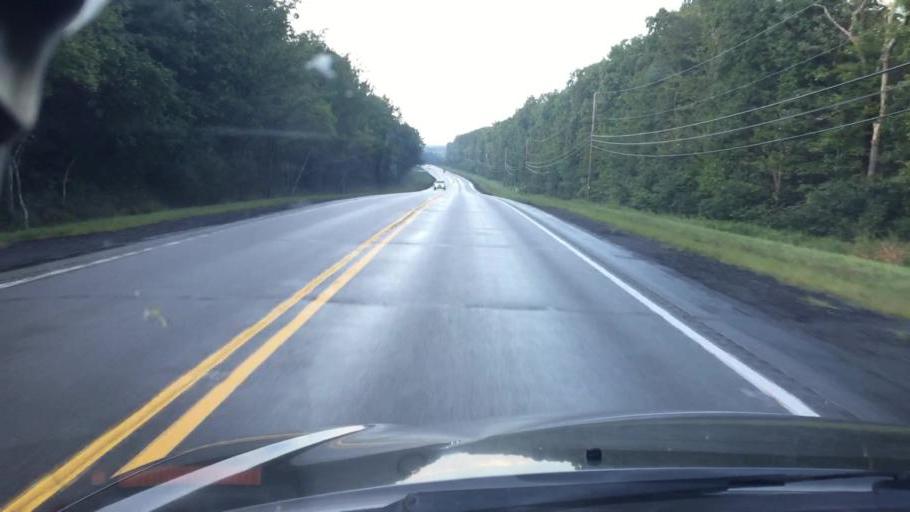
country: US
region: Pennsylvania
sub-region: Carbon County
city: Jim Thorpe
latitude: 40.9166
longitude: -75.6686
